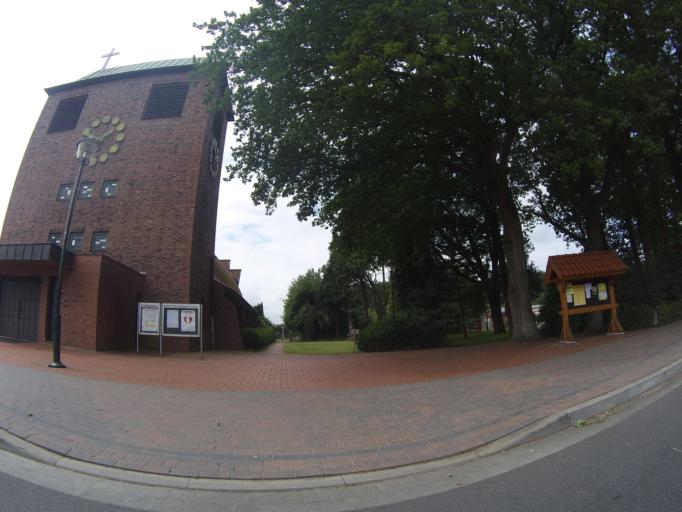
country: DE
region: Lower Saxony
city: Twist
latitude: 52.7096
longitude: 7.0990
